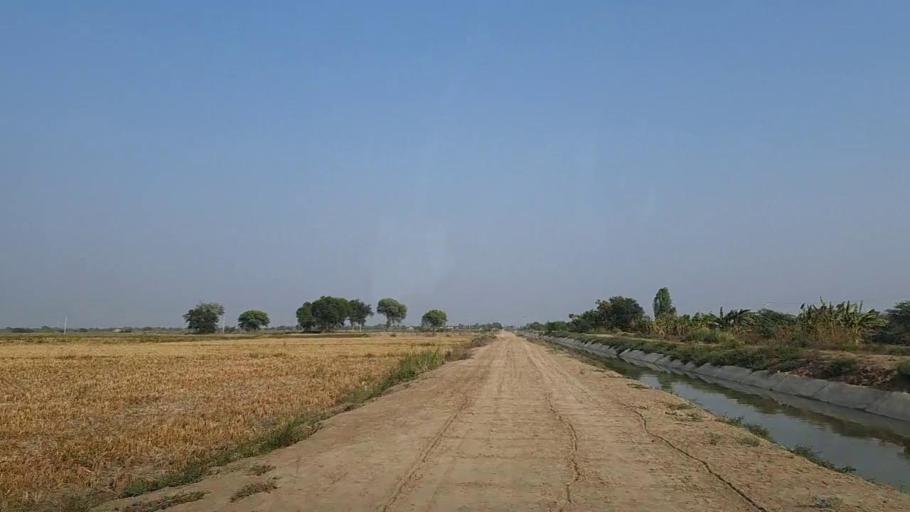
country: PK
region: Sindh
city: Mirpur Sakro
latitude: 24.6155
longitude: 67.7195
